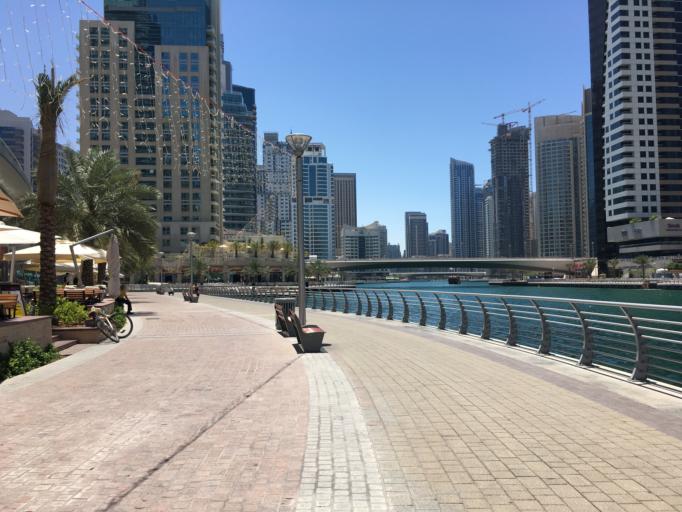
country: AE
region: Dubai
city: Dubai
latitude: 25.0835
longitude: 55.1466
